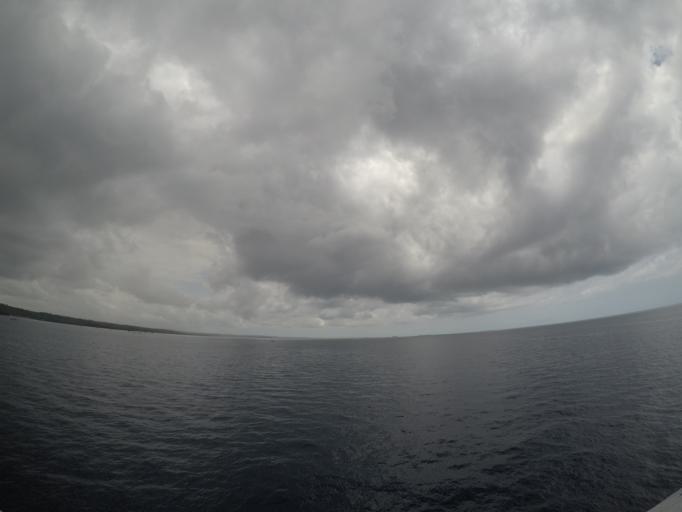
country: TZ
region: Zanzibar North
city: Mkokotoni
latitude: -5.9945
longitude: 39.1752
